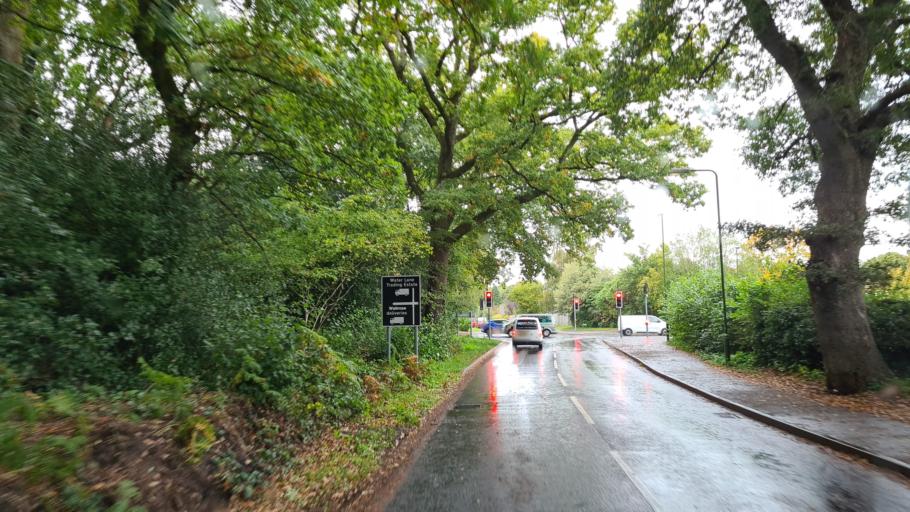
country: GB
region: England
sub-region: West Sussex
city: Storrington
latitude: 50.9226
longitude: -0.4386
